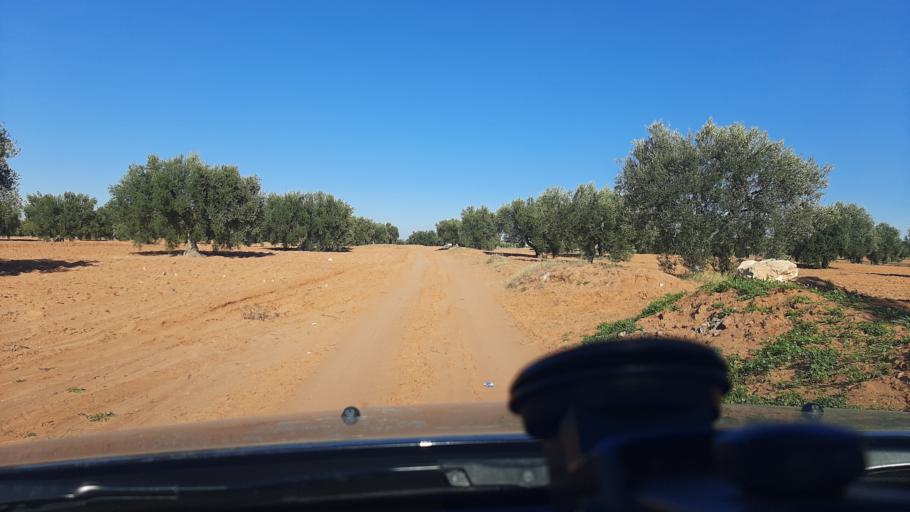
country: TN
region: Safaqis
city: Bi'r `Ali Bin Khalifah
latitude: 35.0049
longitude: 10.0882
